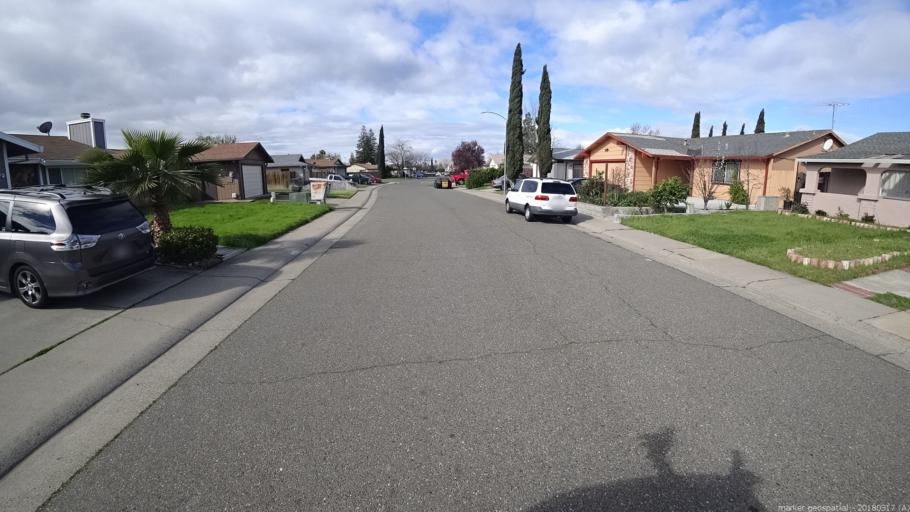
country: US
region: California
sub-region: Sacramento County
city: Florin
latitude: 38.4702
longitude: -121.3959
